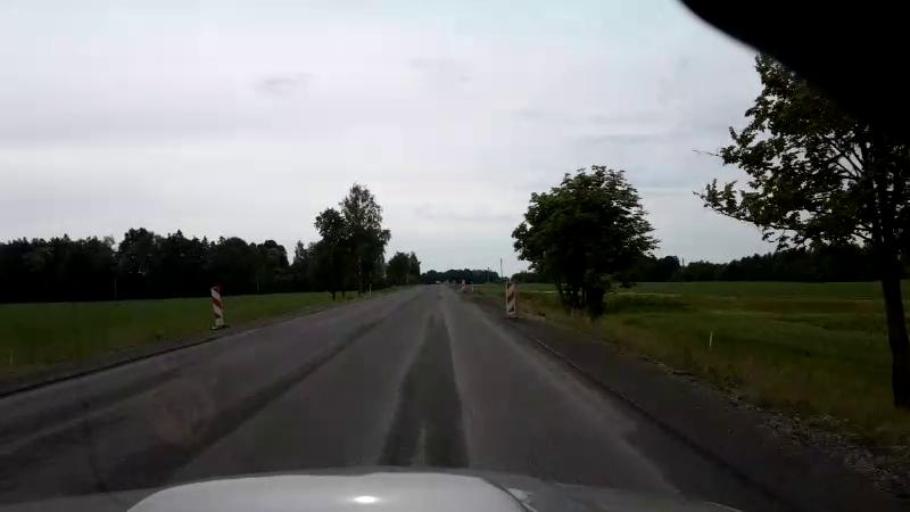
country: LV
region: Bauskas Rajons
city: Bauska
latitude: 56.2986
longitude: 24.3448
